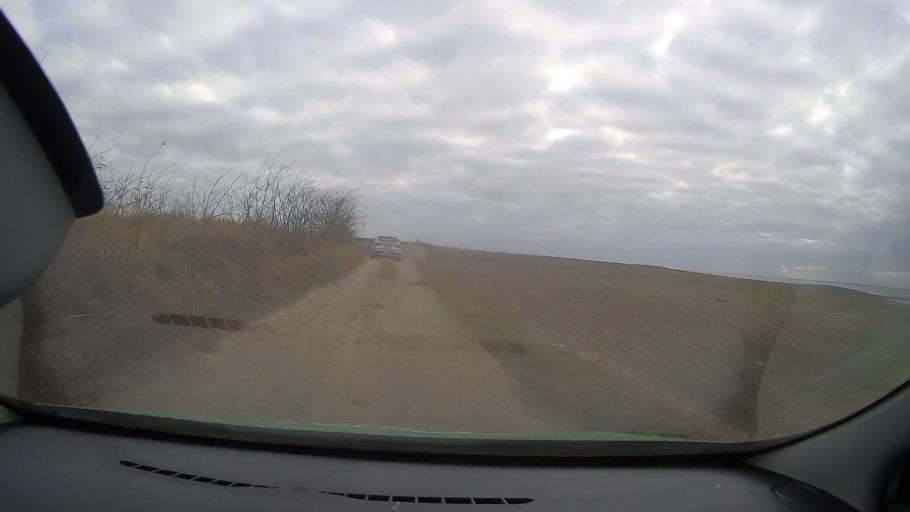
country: RO
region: Tulcea
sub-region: Comuna Jurilovca
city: Jurilovca
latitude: 44.7694
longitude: 28.9109
